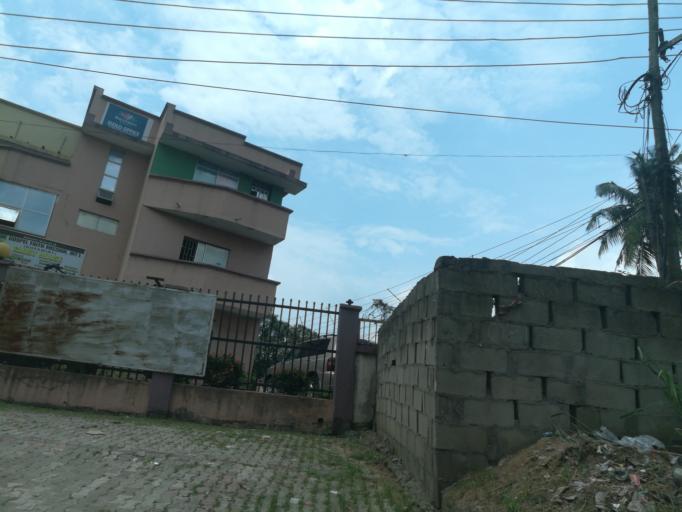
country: NG
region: Lagos
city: Oshodi
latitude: 6.5461
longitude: 3.3327
